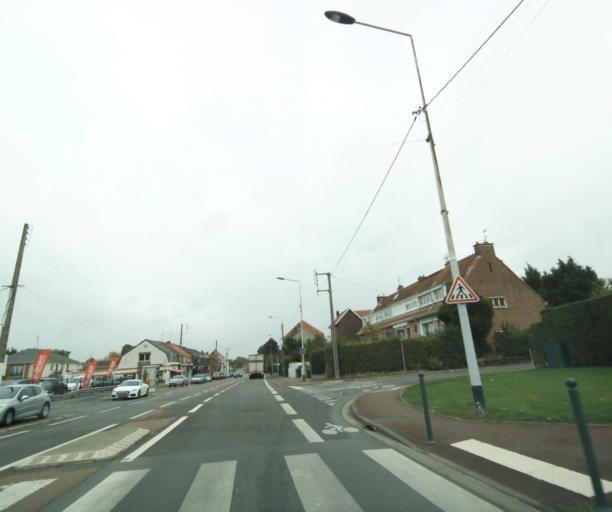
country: FR
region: Nord-Pas-de-Calais
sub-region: Departement du Nord
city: Bondues
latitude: 50.7030
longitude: 3.0975
